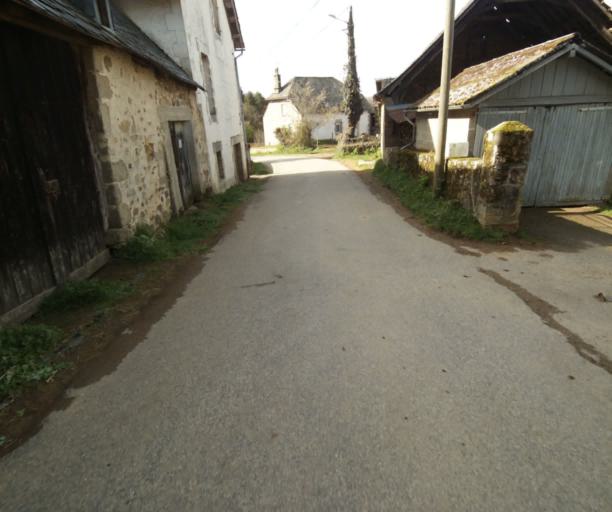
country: FR
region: Limousin
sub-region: Departement de la Correze
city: Laguenne
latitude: 45.2681
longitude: 1.8244
